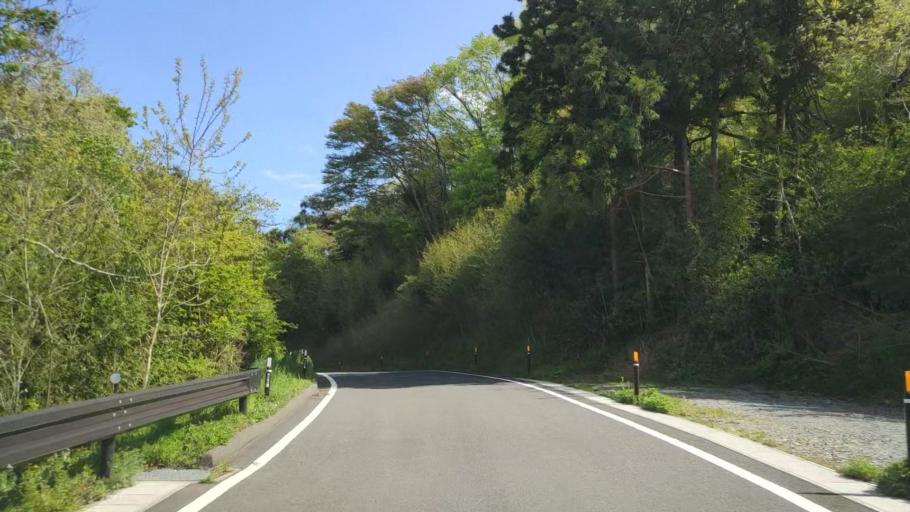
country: JP
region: Miyagi
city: Matsushima
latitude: 38.3384
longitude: 141.1576
